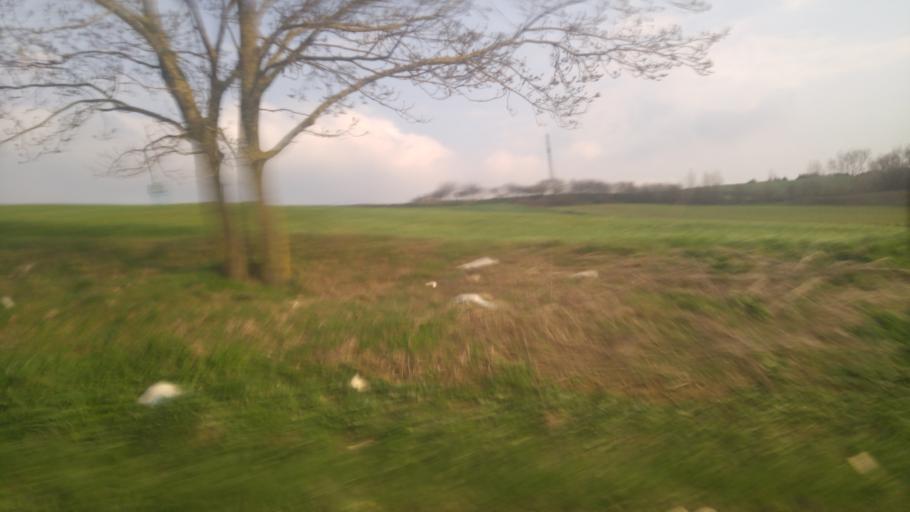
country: TR
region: Istanbul
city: Ortakoy
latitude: 41.1335
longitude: 28.3571
